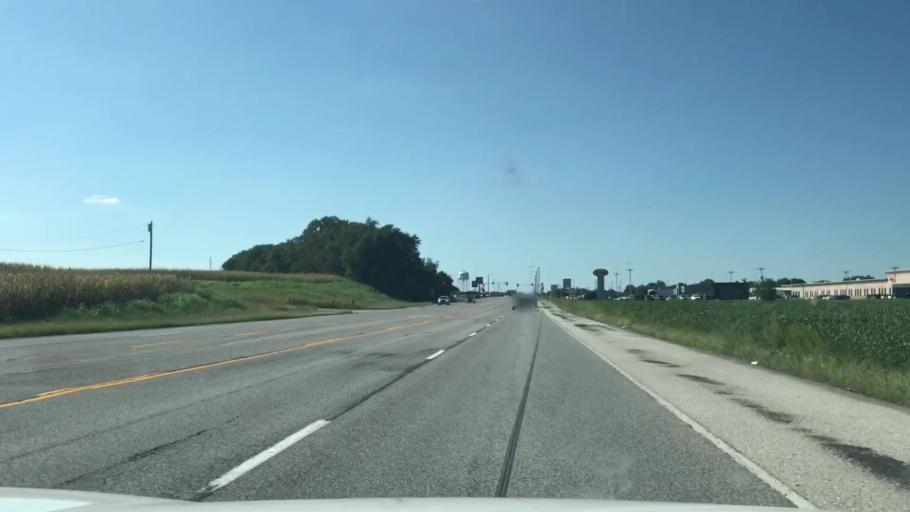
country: US
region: Illinois
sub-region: Madison County
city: Roxana
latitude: 38.8552
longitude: -90.0615
